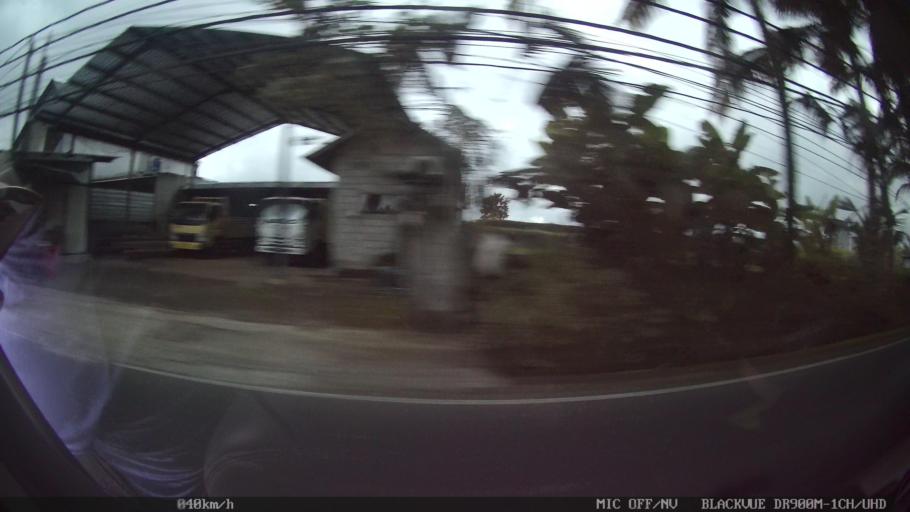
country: ID
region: Bali
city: Bayad
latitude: -8.4544
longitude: 115.2434
